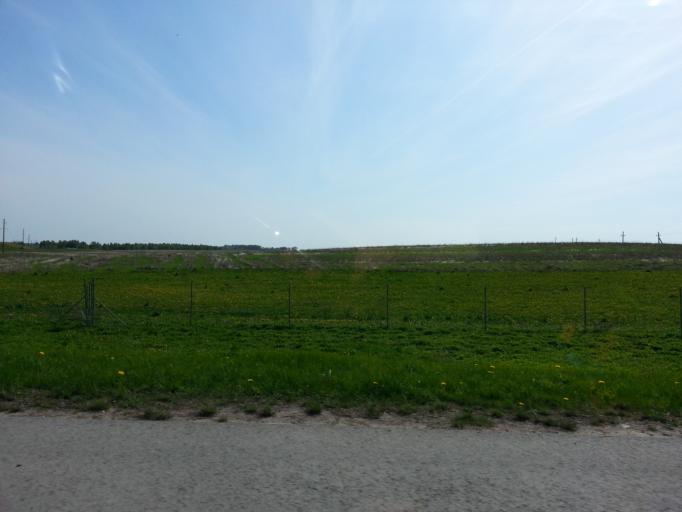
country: LT
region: Vilnius County
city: Ukmerge
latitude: 55.2044
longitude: 24.8161
